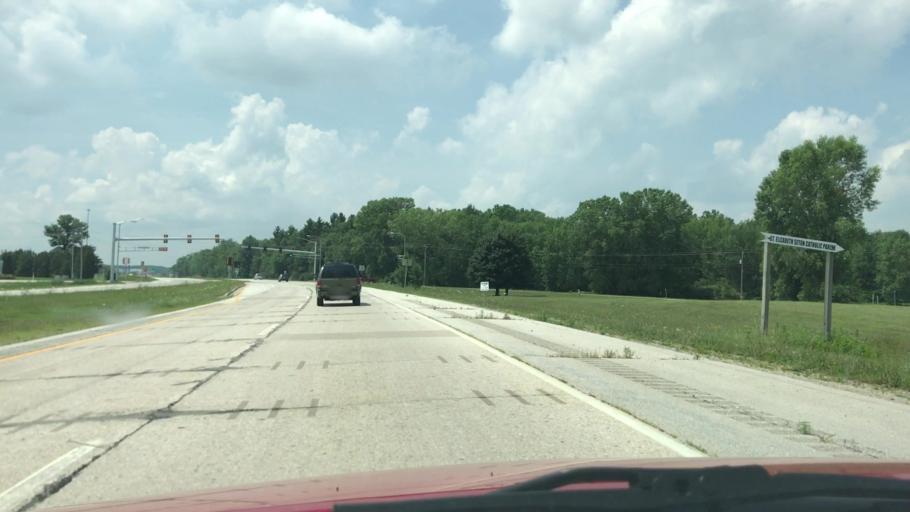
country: US
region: Wisconsin
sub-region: Brown County
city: Ashwaubenon
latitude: 44.4967
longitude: -88.1112
